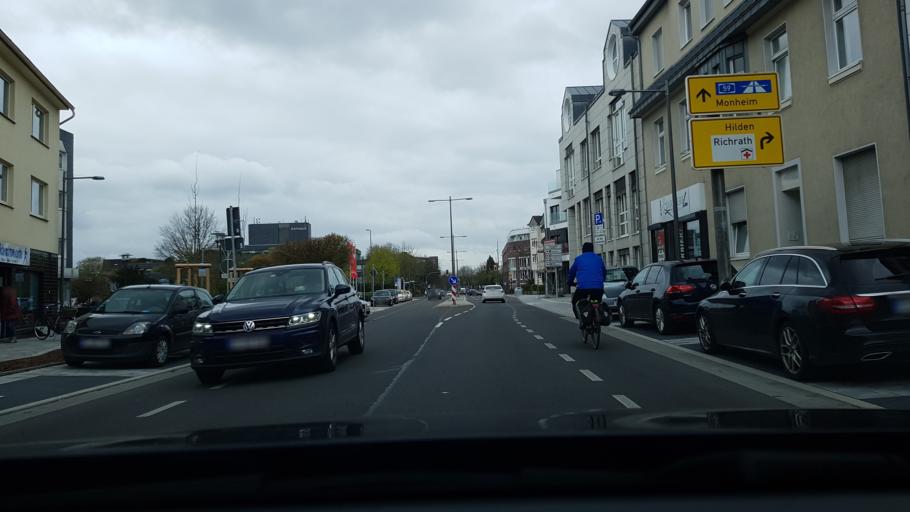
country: DE
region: North Rhine-Westphalia
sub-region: Regierungsbezirk Dusseldorf
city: Langenfeld
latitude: 51.1129
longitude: 6.9546
